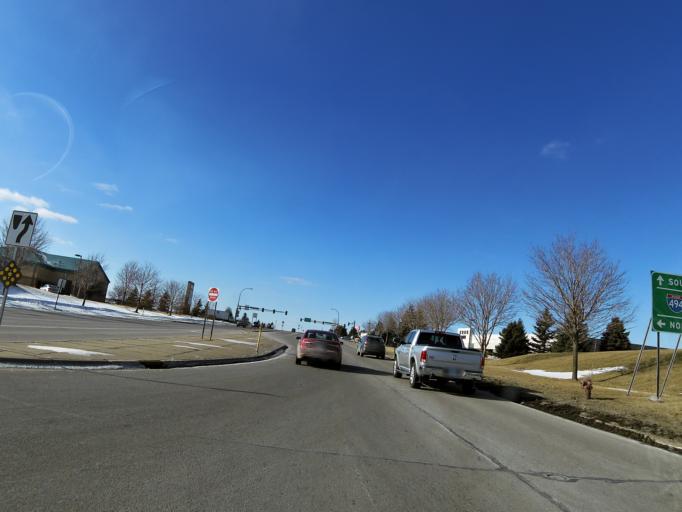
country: US
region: Minnesota
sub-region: Washington County
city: Woodbury
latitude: 44.9135
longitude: -92.9759
